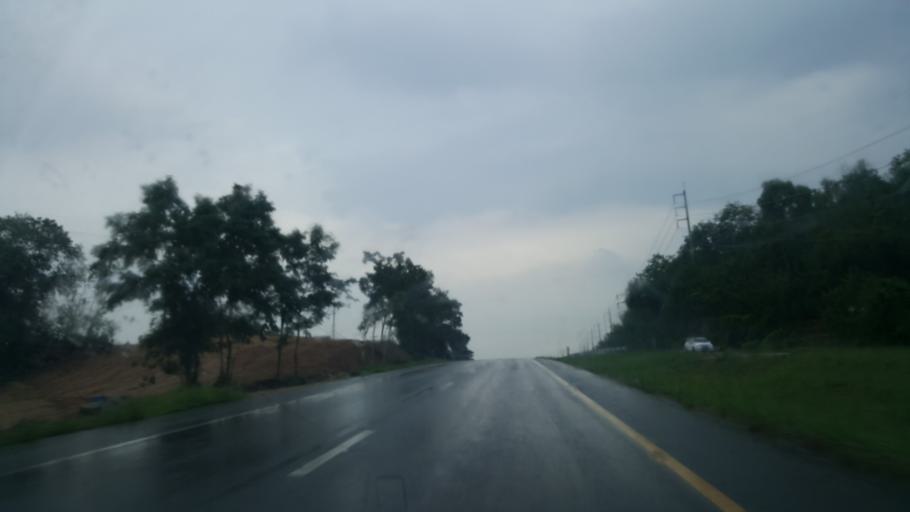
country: TH
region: Chon Buri
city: Ban Talat Bueng
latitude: 12.9872
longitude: 101.0609
